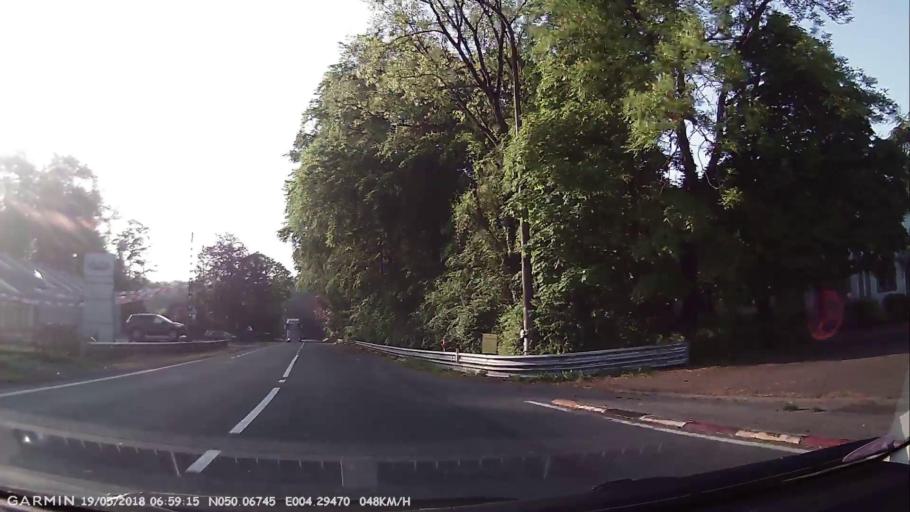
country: BE
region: Wallonia
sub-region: Province du Hainaut
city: Chimay
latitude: 50.0673
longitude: 4.2951
